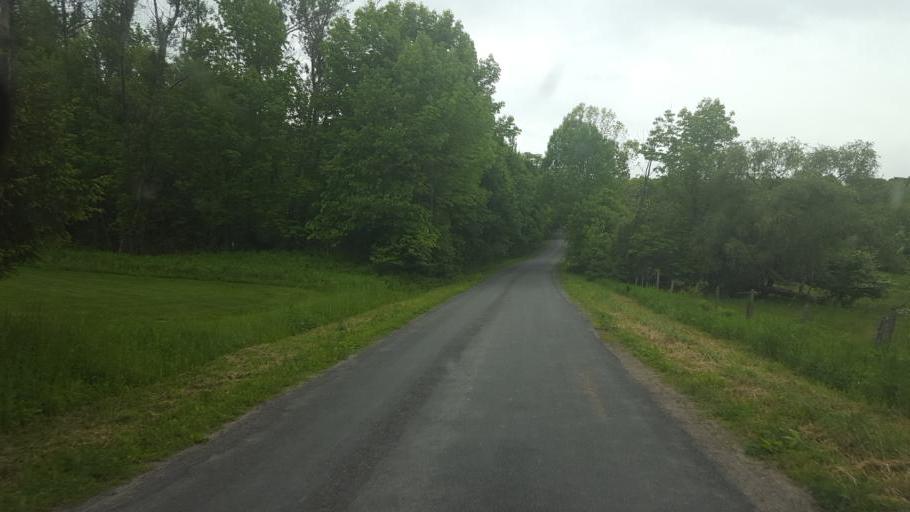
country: US
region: New York
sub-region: Oneida County
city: Chadwicks
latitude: 42.8685
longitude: -75.1761
